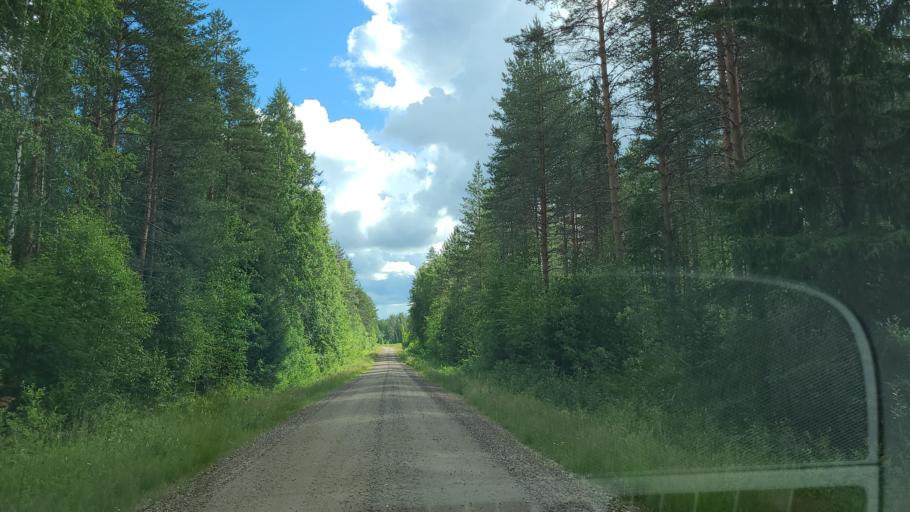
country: FI
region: Northern Savo
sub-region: Koillis-Savo
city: Kaavi
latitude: 63.0273
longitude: 28.7742
